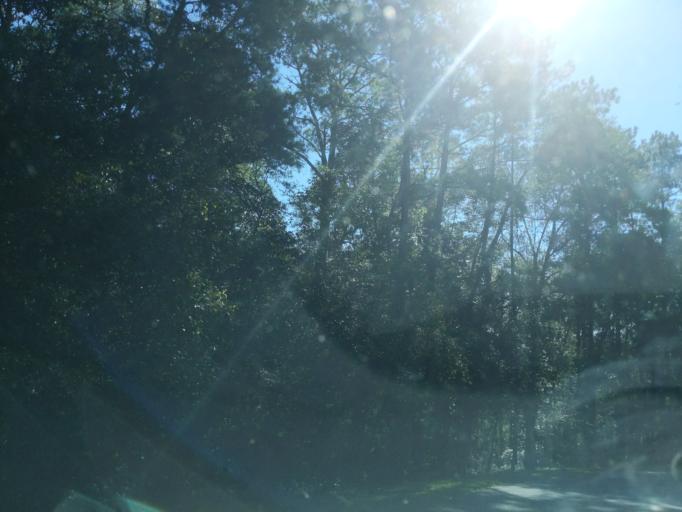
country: US
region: Florida
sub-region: Walton County
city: DeFuniak Springs
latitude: 30.7147
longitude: -85.9299
